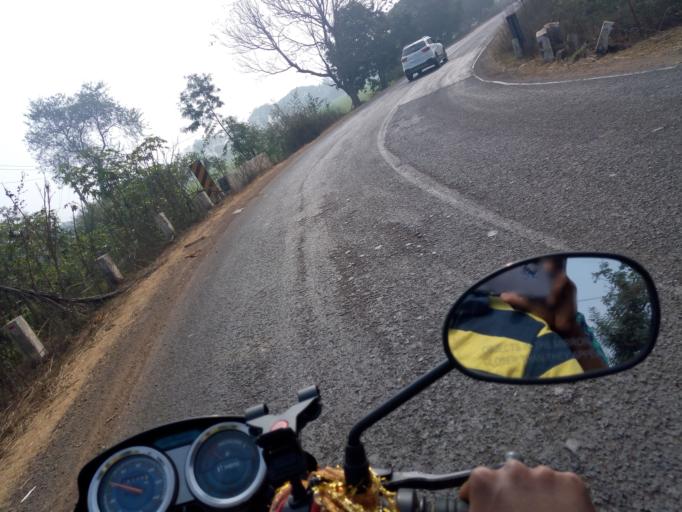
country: IN
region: Andhra Pradesh
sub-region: West Godavari
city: Tadepallegudem
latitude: 16.8004
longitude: 81.4127
